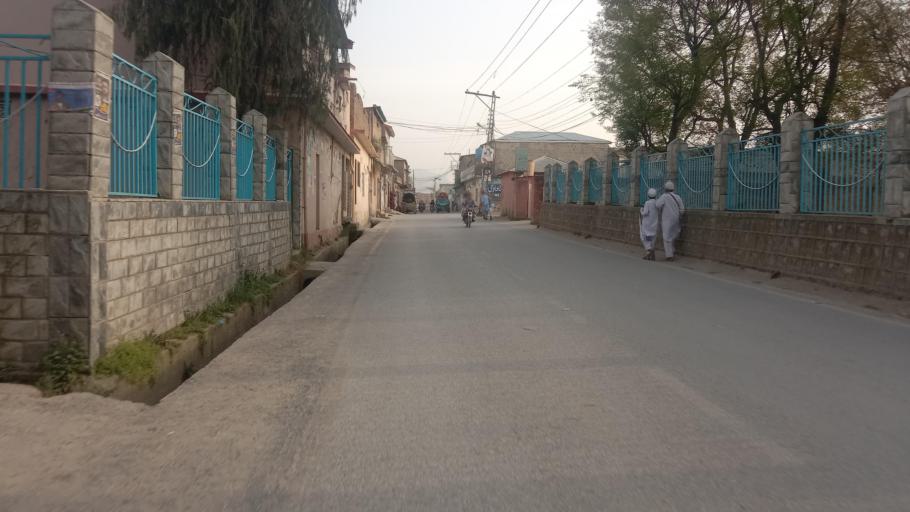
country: PK
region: Khyber Pakhtunkhwa
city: Abbottabad
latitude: 34.1680
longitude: 73.2593
